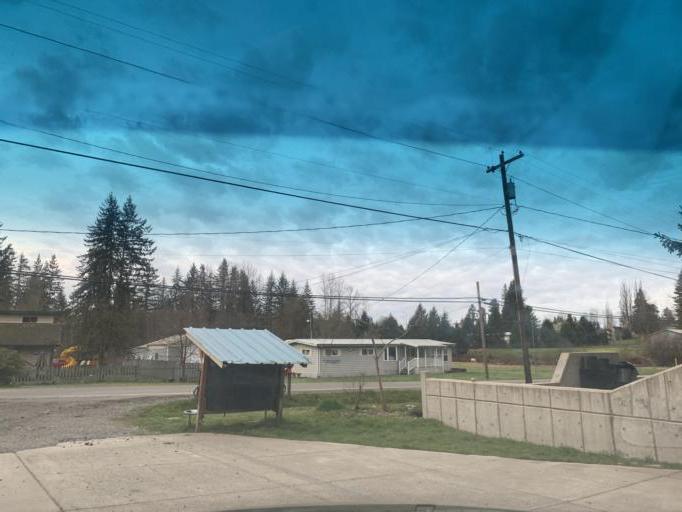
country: US
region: Washington
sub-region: Snohomish County
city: Lake Stevens
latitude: 48.0231
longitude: -122.0496
